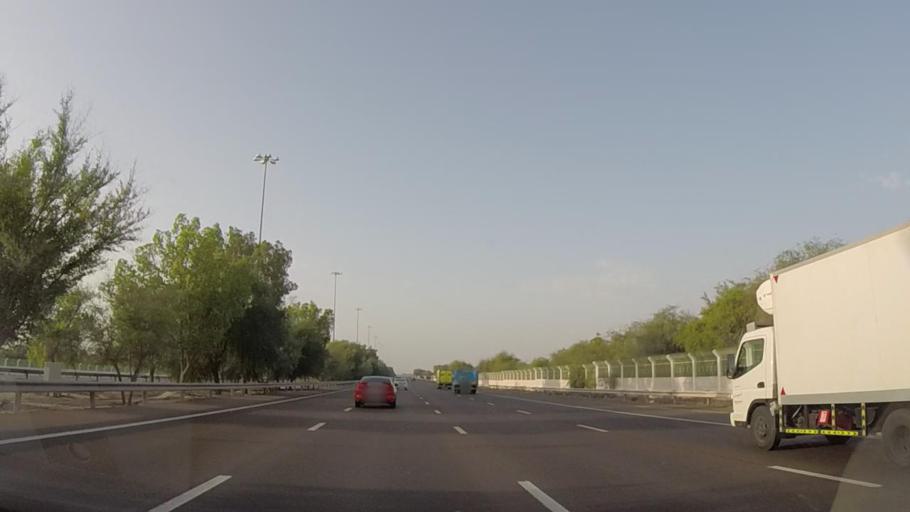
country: AE
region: Dubai
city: Dubai
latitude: 24.8239
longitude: 54.8780
